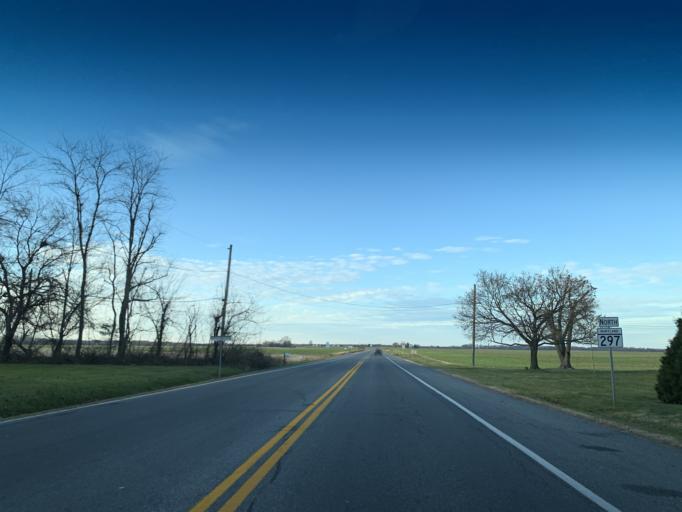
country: US
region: Maryland
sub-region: Kent County
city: Chestertown
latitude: 39.2401
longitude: -76.0674
